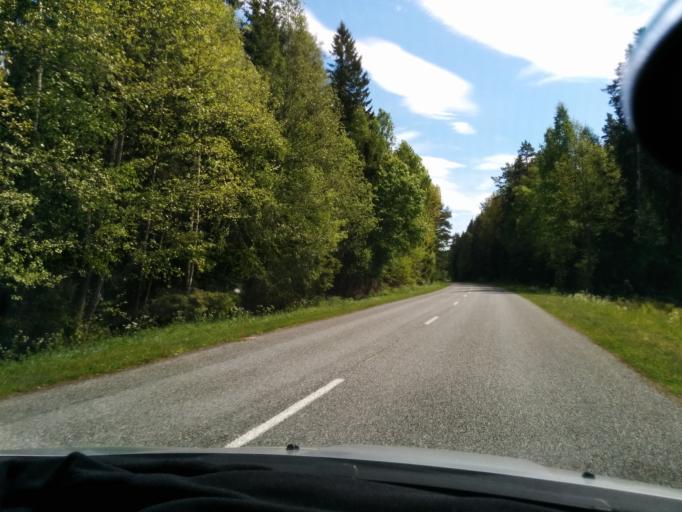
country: EE
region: Harju
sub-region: Loksa linn
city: Loksa
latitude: 59.5676
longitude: 25.9399
